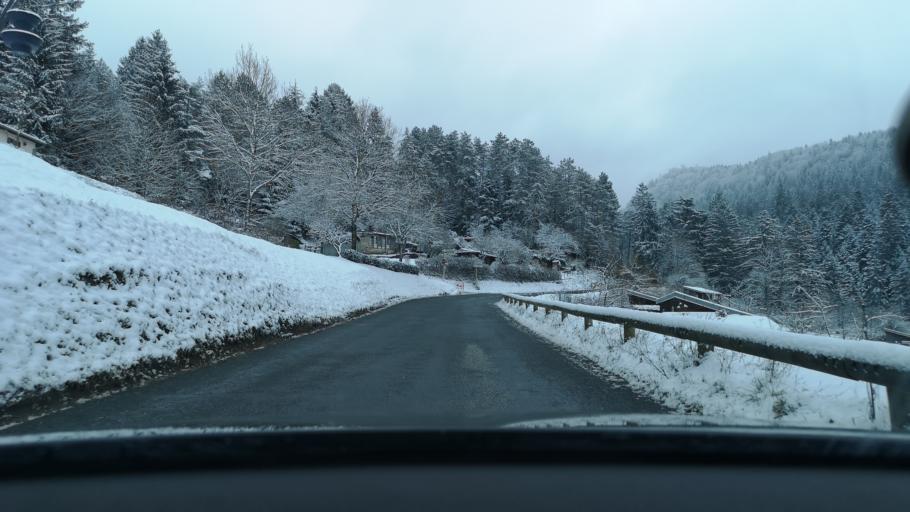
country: FR
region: Rhone-Alpes
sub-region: Departement de l'Ain
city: Oyonnax
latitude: 46.2565
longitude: 5.6662
